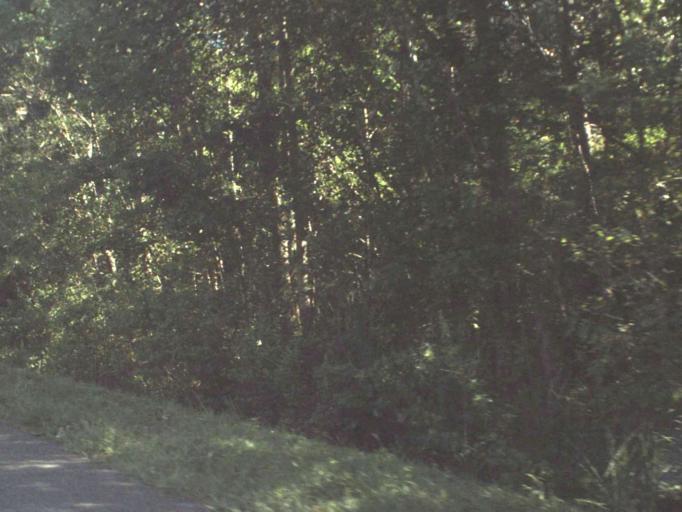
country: US
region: Florida
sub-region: Lake County
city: Four Corners
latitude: 28.3705
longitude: -81.8218
